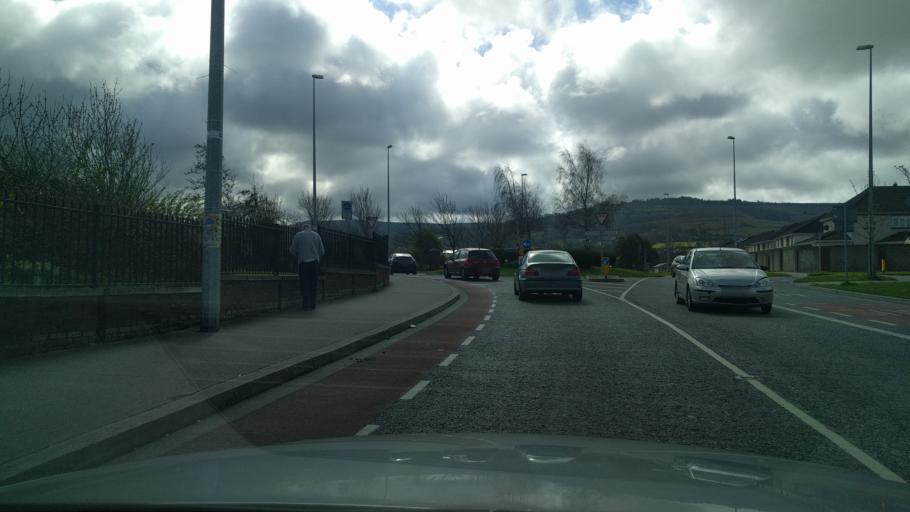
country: IE
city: Knocklyon
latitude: 53.2755
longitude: -6.3311
